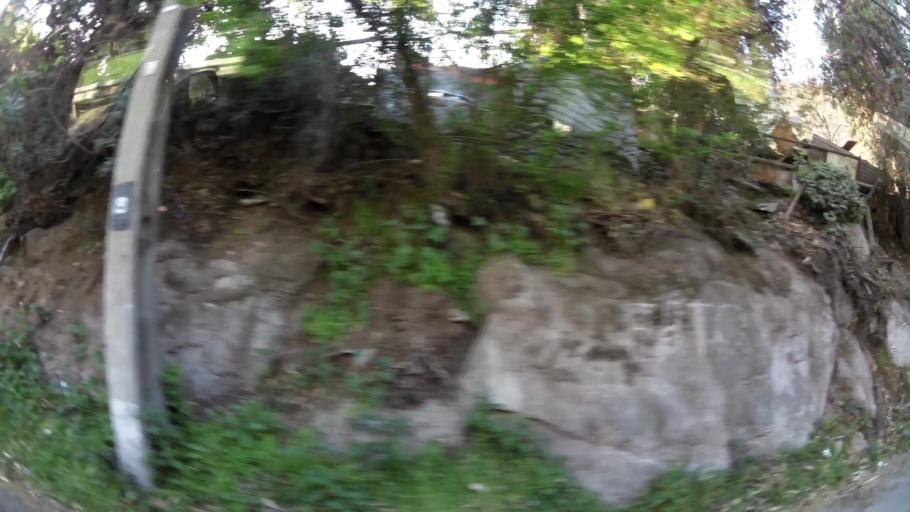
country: CL
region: Santiago Metropolitan
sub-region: Provincia de Santiago
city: Villa Presidente Frei, Nunoa, Santiago, Chile
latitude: -33.3621
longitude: -70.4978
